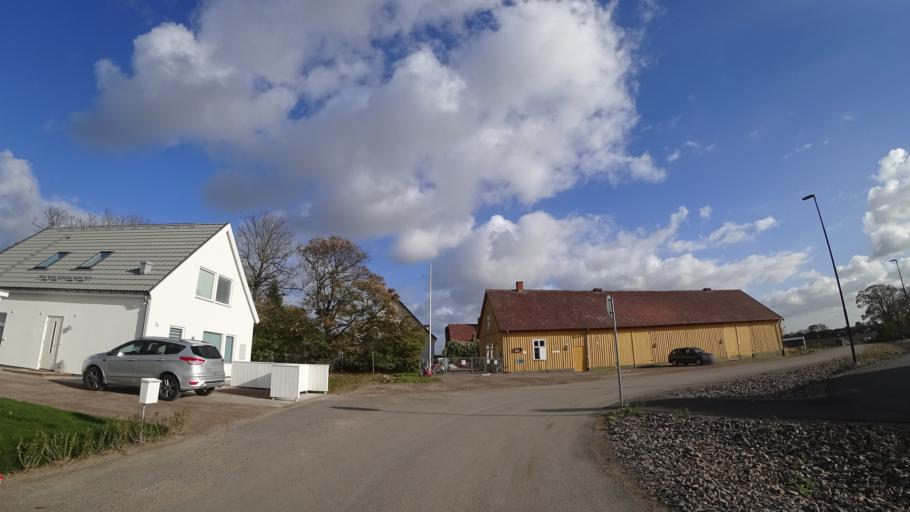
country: SE
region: Skane
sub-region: Staffanstorps Kommun
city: Hjaerup
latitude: 55.6254
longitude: 13.1290
